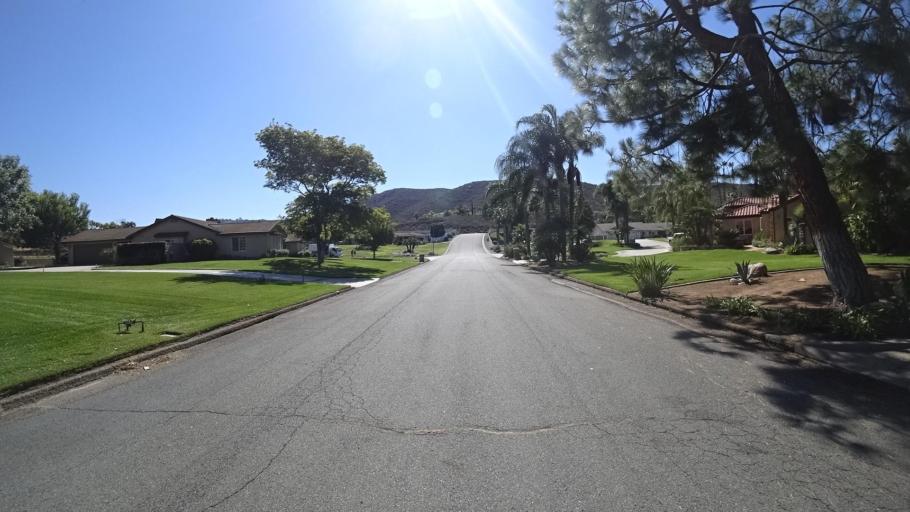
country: US
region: California
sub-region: San Diego County
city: Rancho San Diego
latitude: 32.7424
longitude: -116.9038
